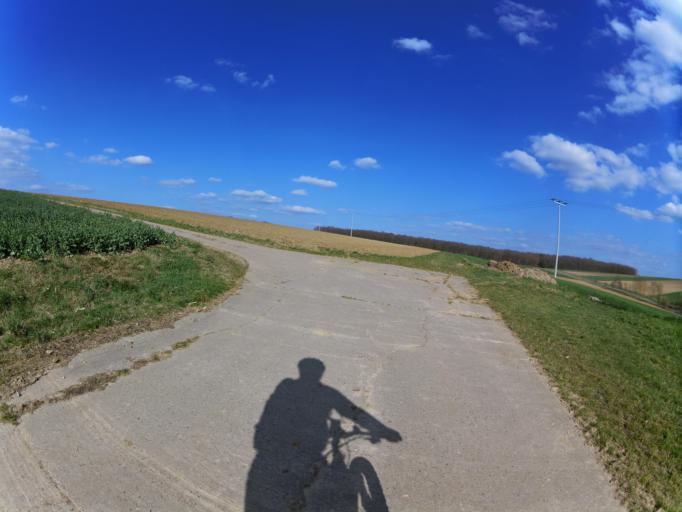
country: DE
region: Bavaria
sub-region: Regierungsbezirk Unterfranken
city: Prosselsheim
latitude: 49.8420
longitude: 10.1535
